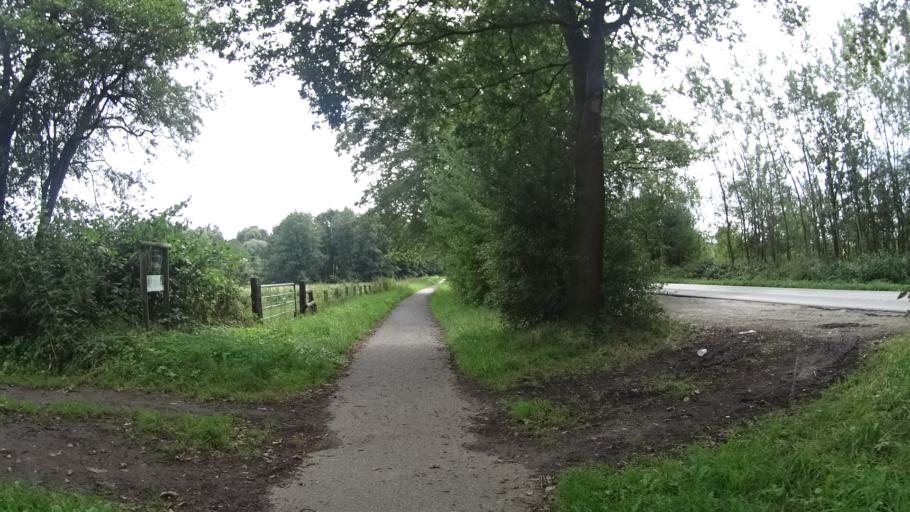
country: DE
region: Hamburg
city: Duvenstedt
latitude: 53.7218
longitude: 10.1102
